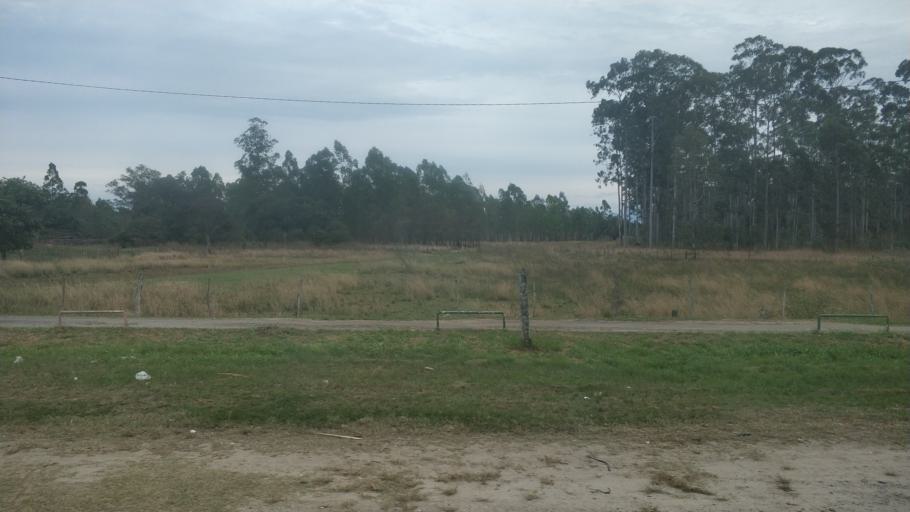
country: BR
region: Rio de Janeiro
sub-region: Seropedica
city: Seropedica
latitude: -22.7895
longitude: -43.6527
